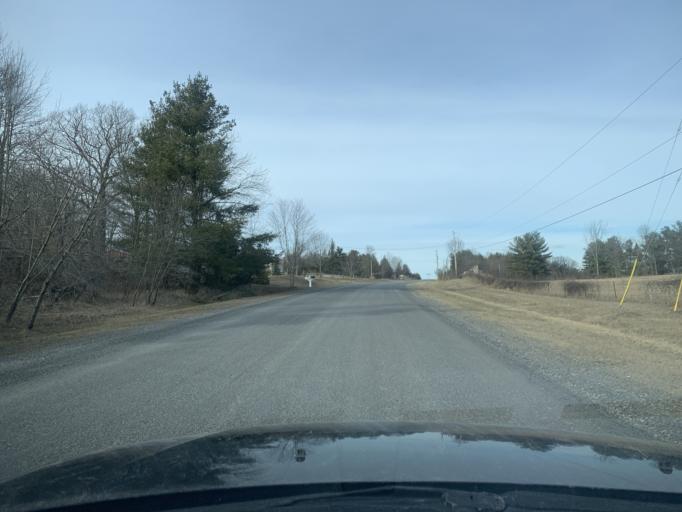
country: CA
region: Ontario
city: Greater Napanee
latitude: 44.4516
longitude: -77.0653
